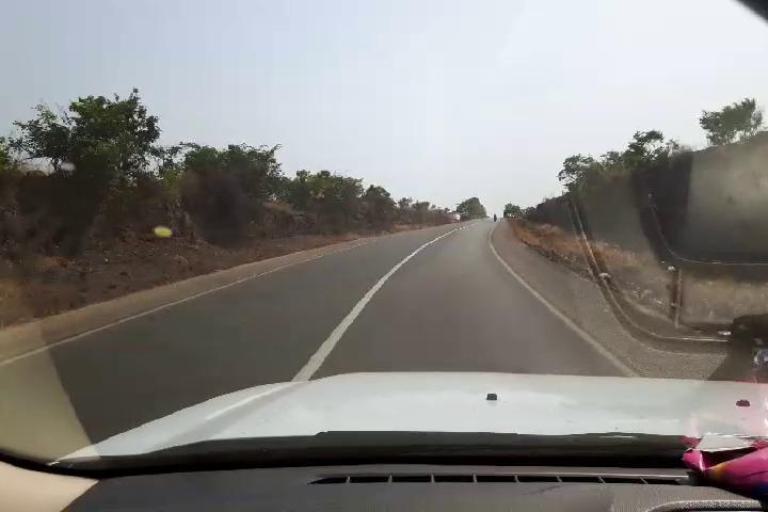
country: SL
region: Western Area
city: Waterloo
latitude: 8.2065
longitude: -13.1086
